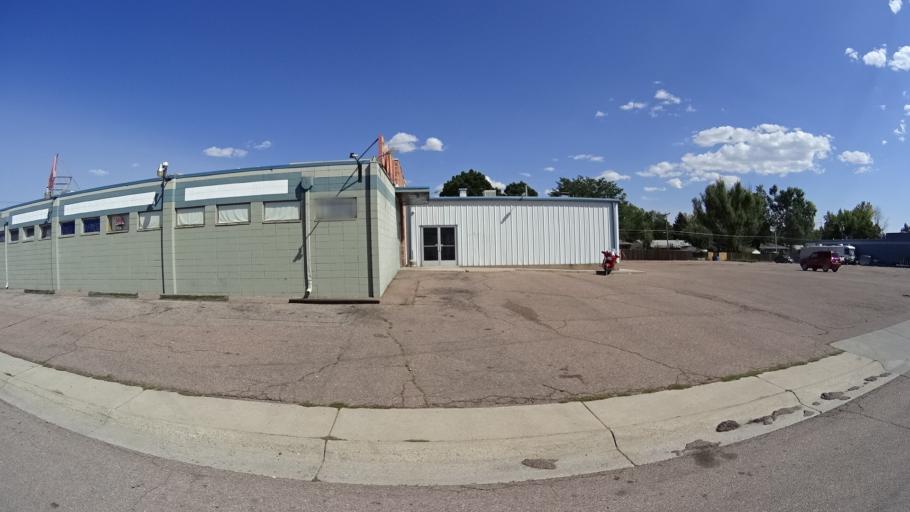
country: US
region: Colorado
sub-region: El Paso County
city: Colorado Springs
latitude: 38.8717
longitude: -104.8113
